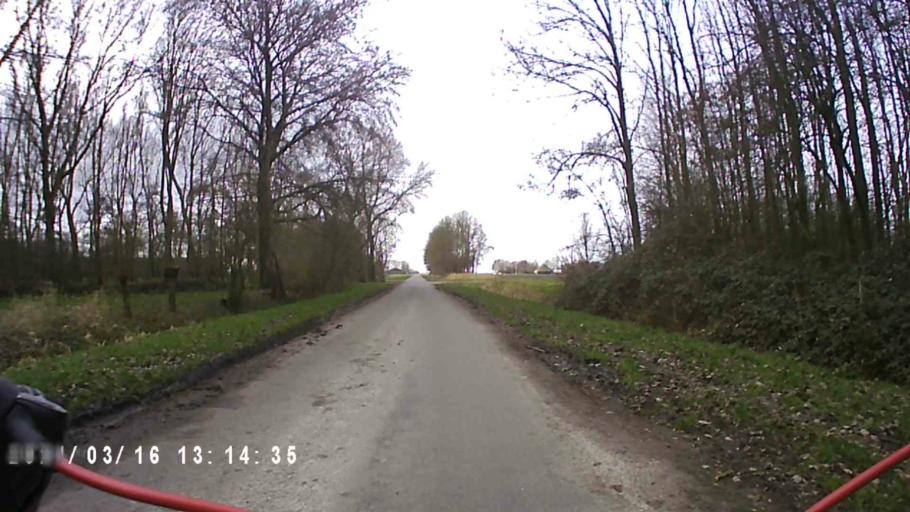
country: NL
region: Friesland
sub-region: Gemeente Het Bildt
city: Minnertsga
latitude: 53.2398
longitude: 5.6024
